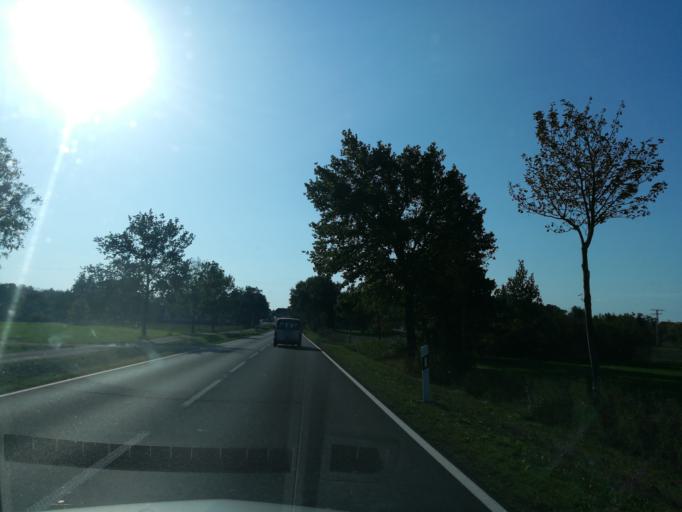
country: DE
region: Saxony-Anhalt
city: Wahlitz
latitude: 52.1222
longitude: 11.7629
